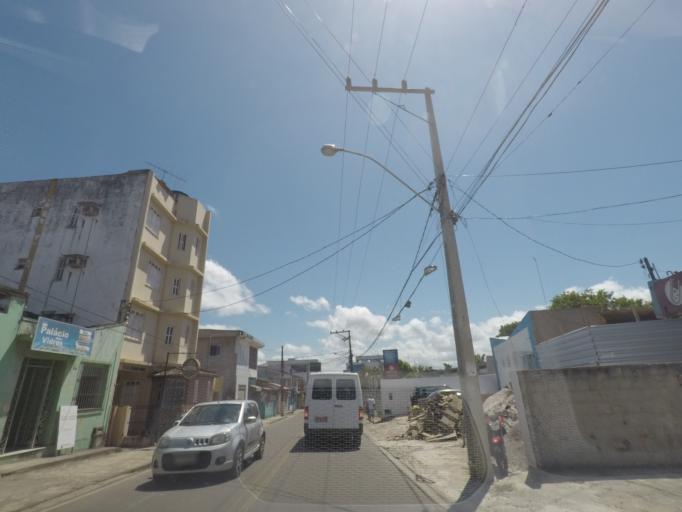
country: BR
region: Bahia
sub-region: Valenca
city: Valenca
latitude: -13.3741
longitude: -39.0728
